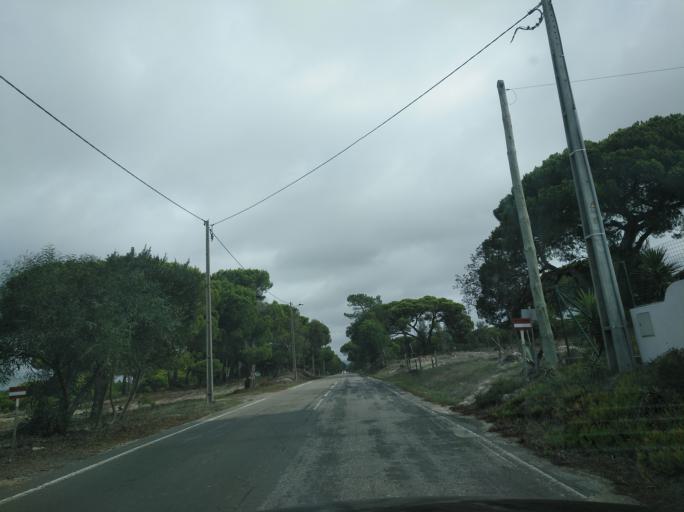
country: PT
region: Setubal
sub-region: Santiago do Cacem
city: Santo Andre
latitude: 38.1320
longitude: -8.7744
